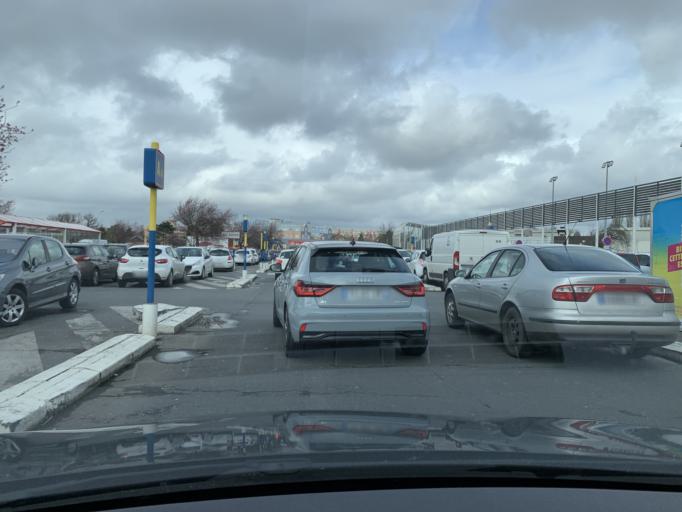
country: FR
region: Nord-Pas-de-Calais
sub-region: Departement du Nord
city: Dechy
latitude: 50.3417
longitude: 3.0982
